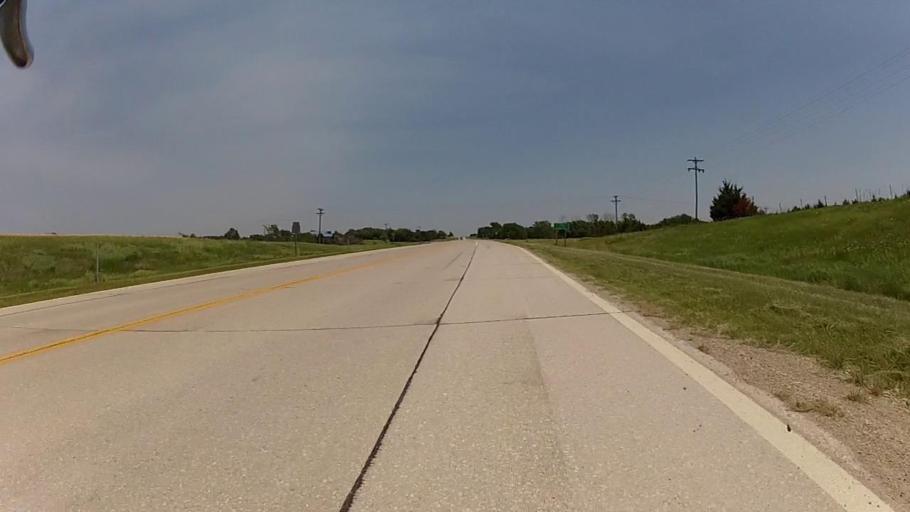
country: US
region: Kansas
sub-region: Cowley County
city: Arkansas City
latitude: 37.0570
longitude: -97.2395
